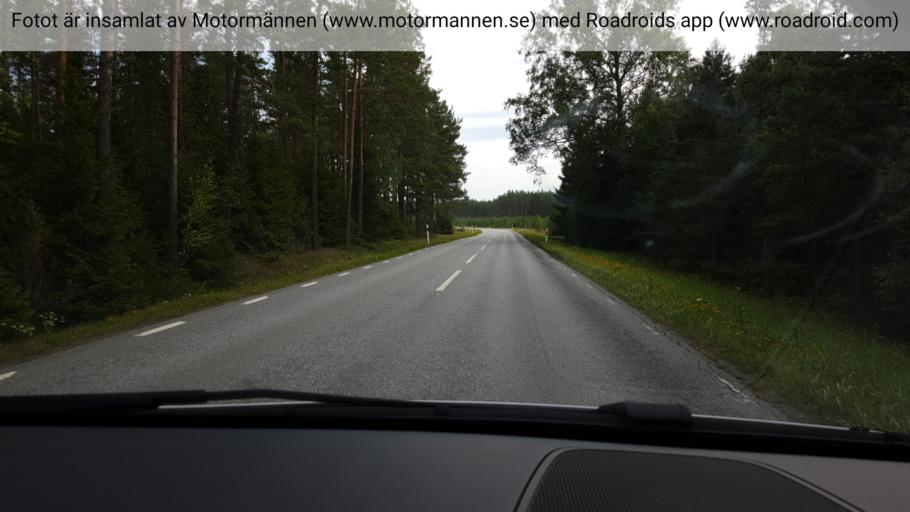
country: SE
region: Uppsala
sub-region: Osthammars Kommun
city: OEsthammar
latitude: 60.2125
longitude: 18.3654
